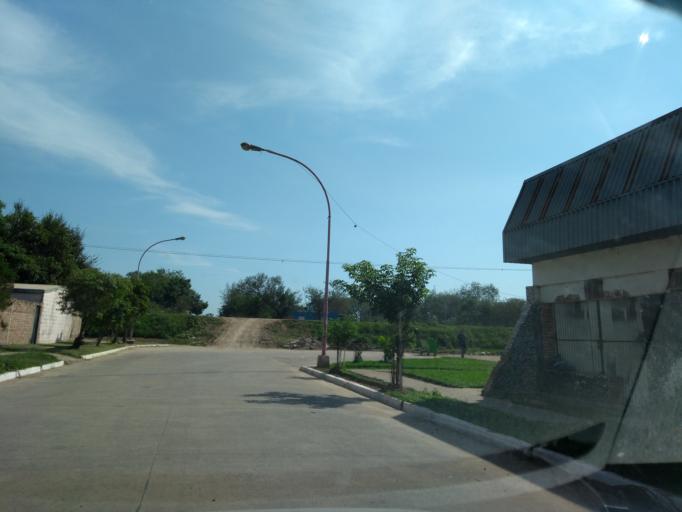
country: AR
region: Chaco
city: Barranqueras
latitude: -27.4605
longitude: -58.9493
